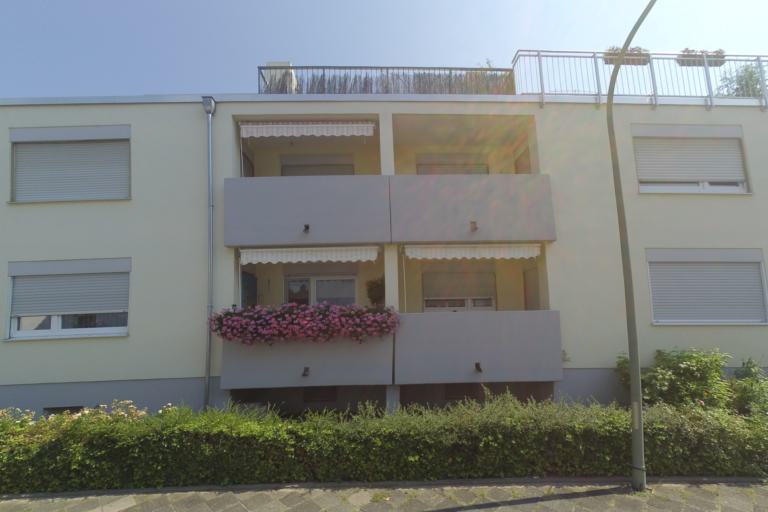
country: DE
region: Rheinland-Pfalz
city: Gartenstadt
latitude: 49.4877
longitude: 8.3723
